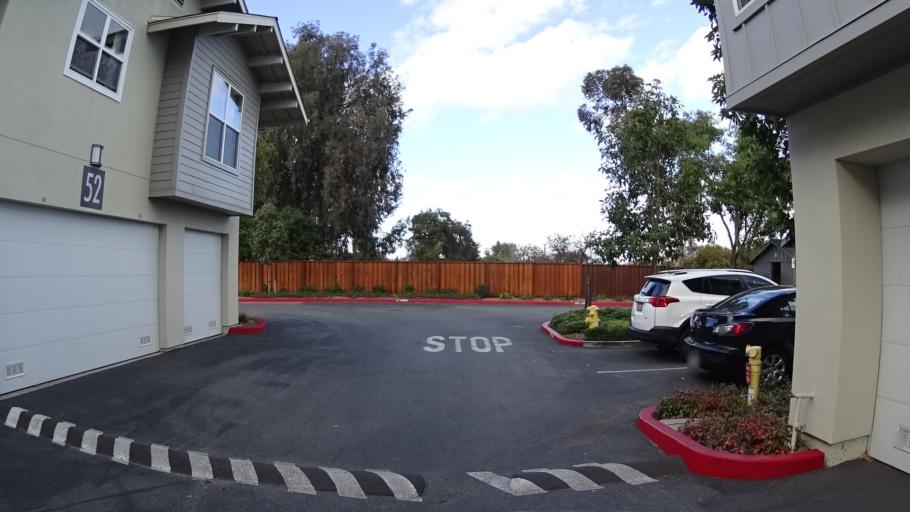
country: US
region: California
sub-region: Santa Clara County
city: Cupertino
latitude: 37.3357
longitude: -122.0411
